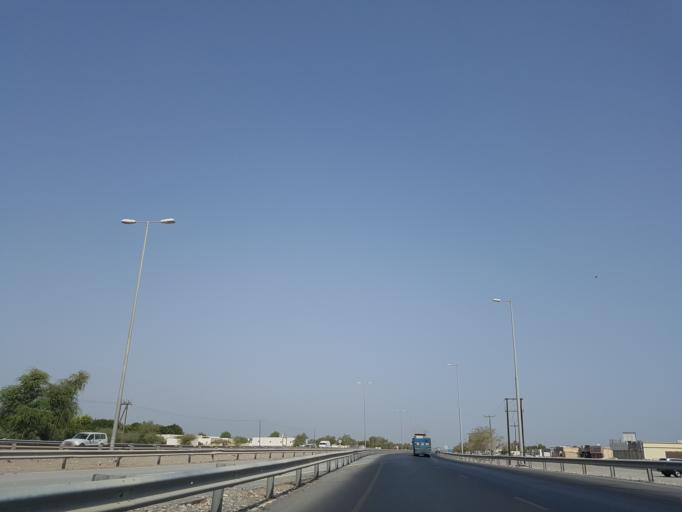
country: OM
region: Al Batinah
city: As Suwayq
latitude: 23.7644
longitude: 57.5505
